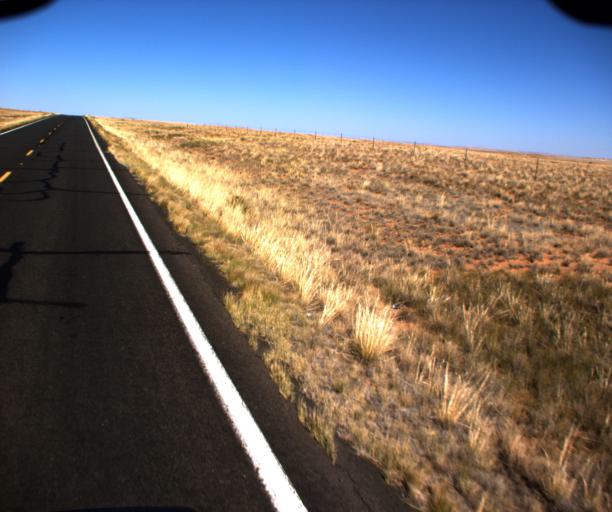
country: US
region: Arizona
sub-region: Navajo County
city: First Mesa
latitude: 35.6300
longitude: -110.4818
